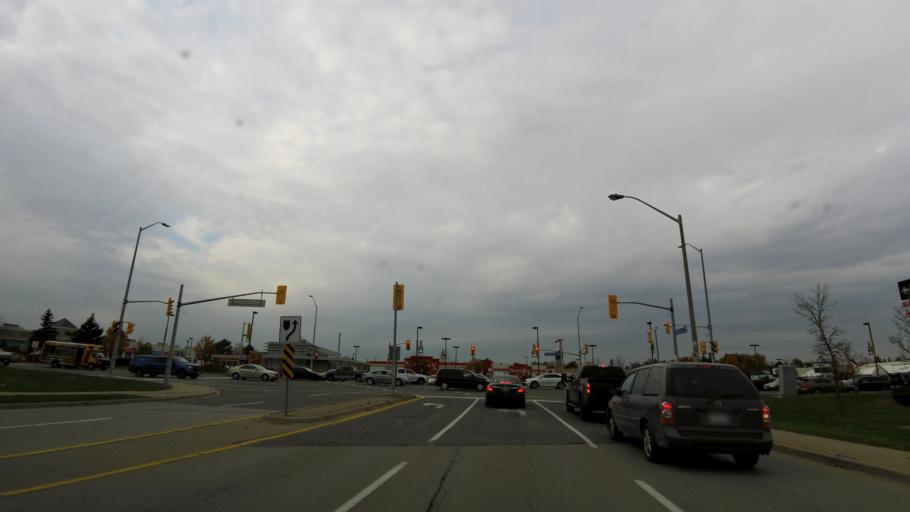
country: CA
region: Ontario
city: Mississauga
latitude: 43.5201
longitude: -79.6837
